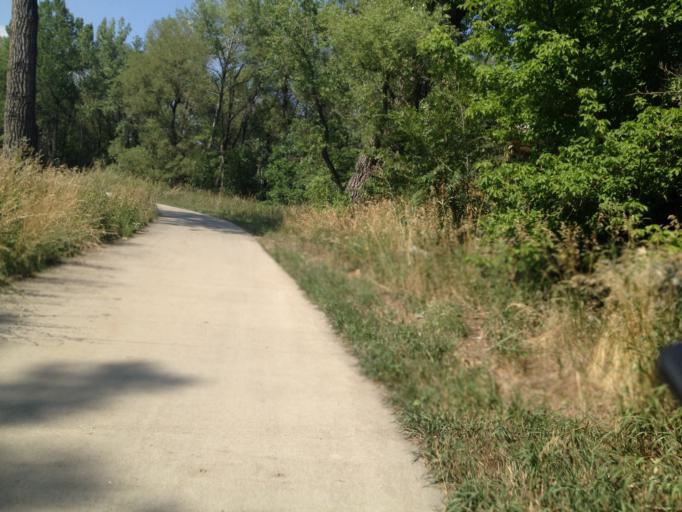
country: US
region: Colorado
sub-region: Boulder County
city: Boulder
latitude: 40.0153
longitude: -105.2147
